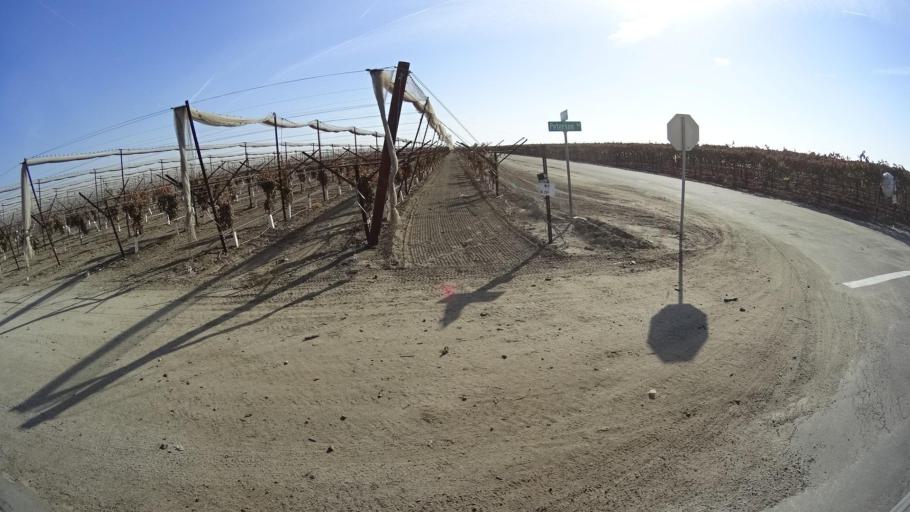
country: US
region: California
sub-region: Kern County
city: McFarland
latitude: 35.7033
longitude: -119.2674
